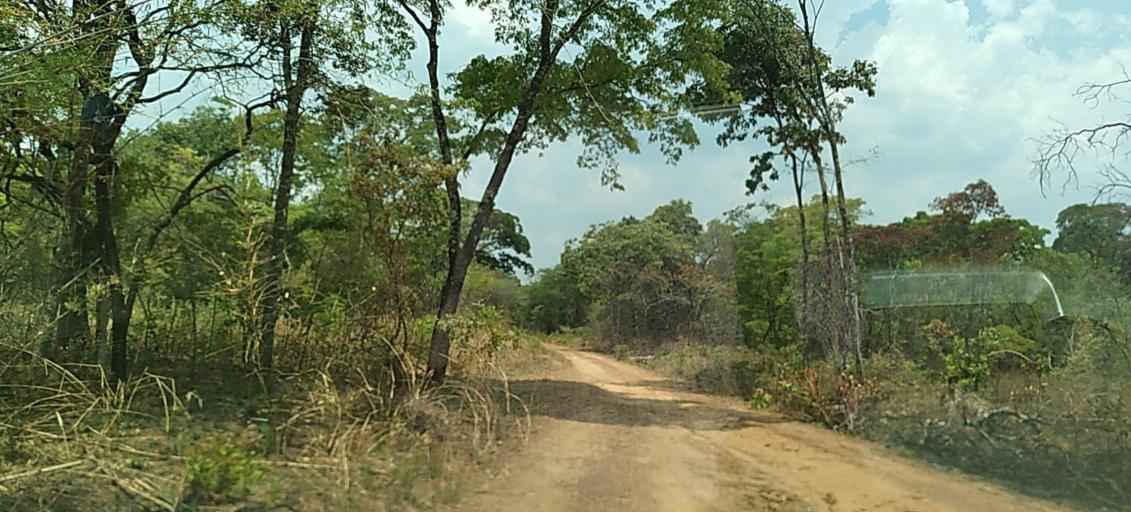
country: ZM
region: Copperbelt
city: Chingola
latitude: -12.7891
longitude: 27.6530
